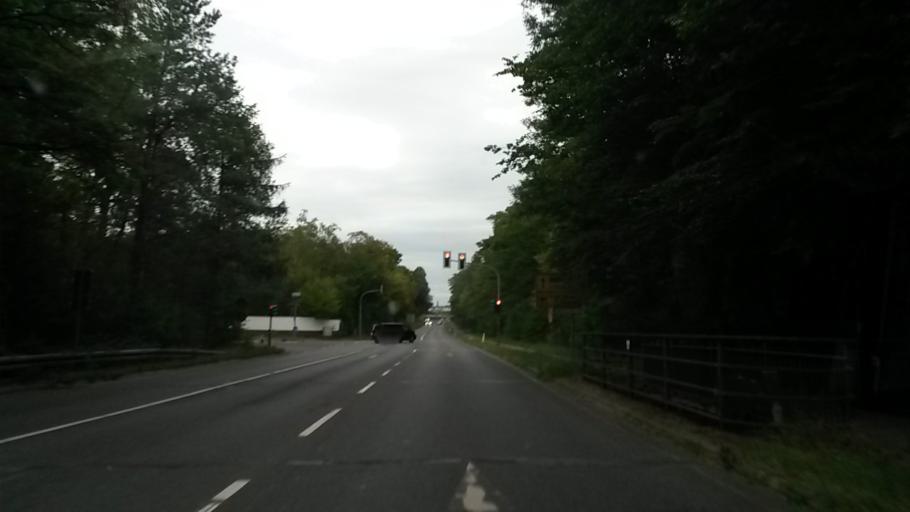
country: DE
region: North Rhine-Westphalia
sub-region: Regierungsbezirk Koln
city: Rath
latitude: 50.9443
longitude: 7.1184
